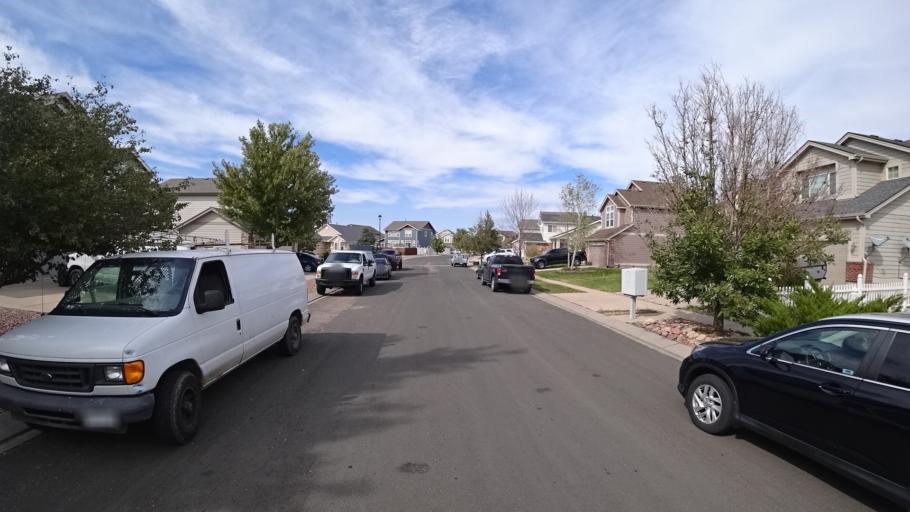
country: US
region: Colorado
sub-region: El Paso County
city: Cimarron Hills
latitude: 38.9100
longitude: -104.6983
